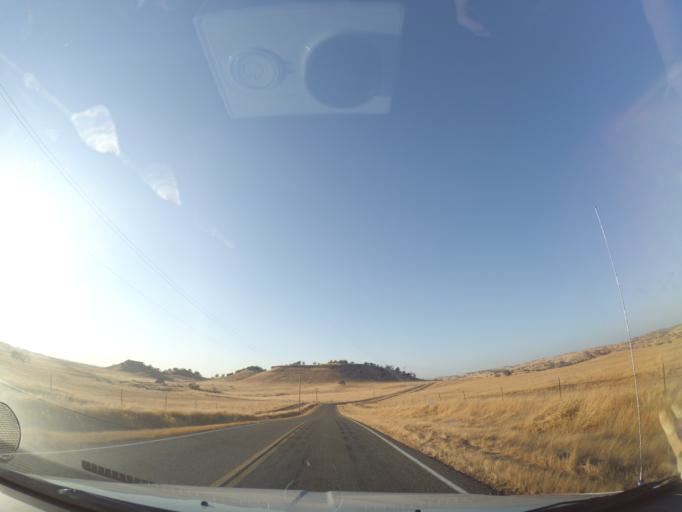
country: US
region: California
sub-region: Merced County
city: Planada
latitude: 37.5038
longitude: -120.3153
